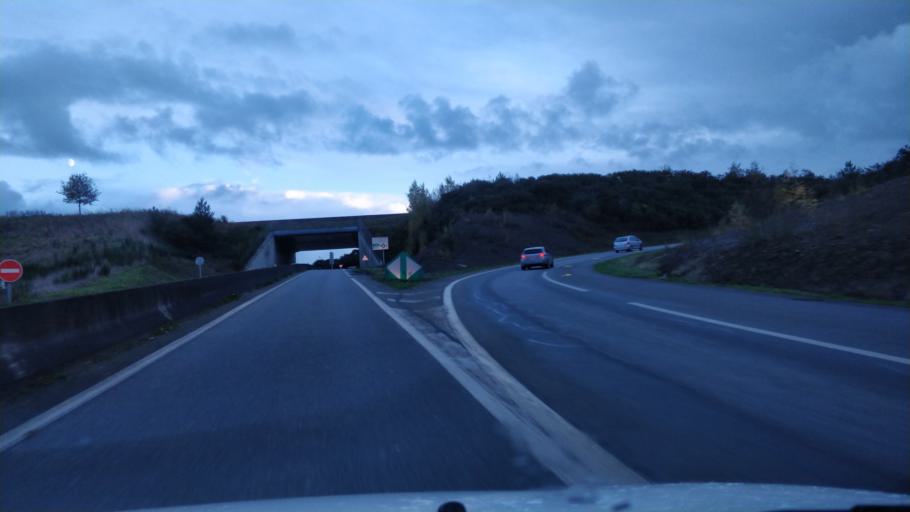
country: FR
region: Brittany
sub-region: Departement du Morbihan
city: Pontivy
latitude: 48.0815
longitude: -2.9420
